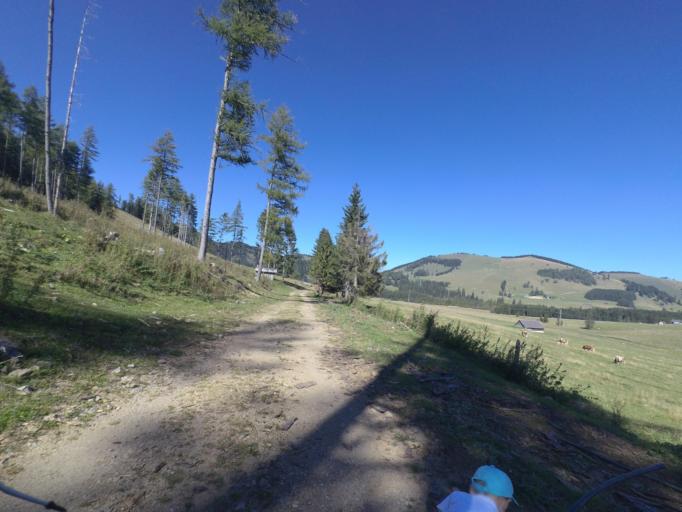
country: AT
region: Styria
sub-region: Politischer Bezirk Weiz
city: Passail
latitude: 47.3408
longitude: 15.4656
